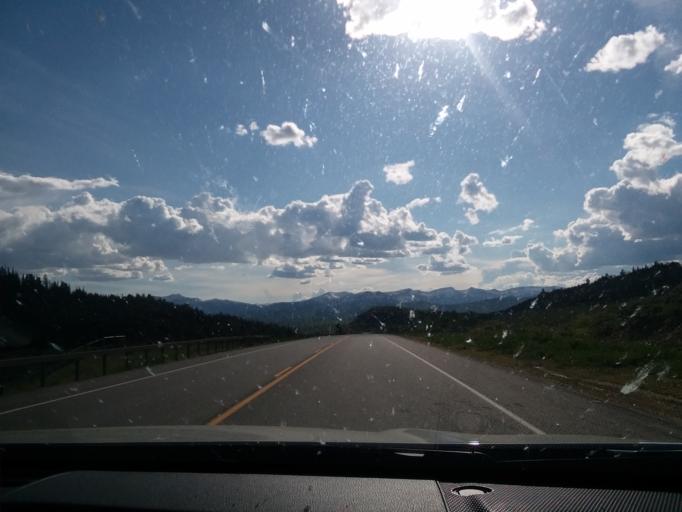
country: US
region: Wyoming
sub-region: Teton County
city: Hoback
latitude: 43.1554
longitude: -110.3135
